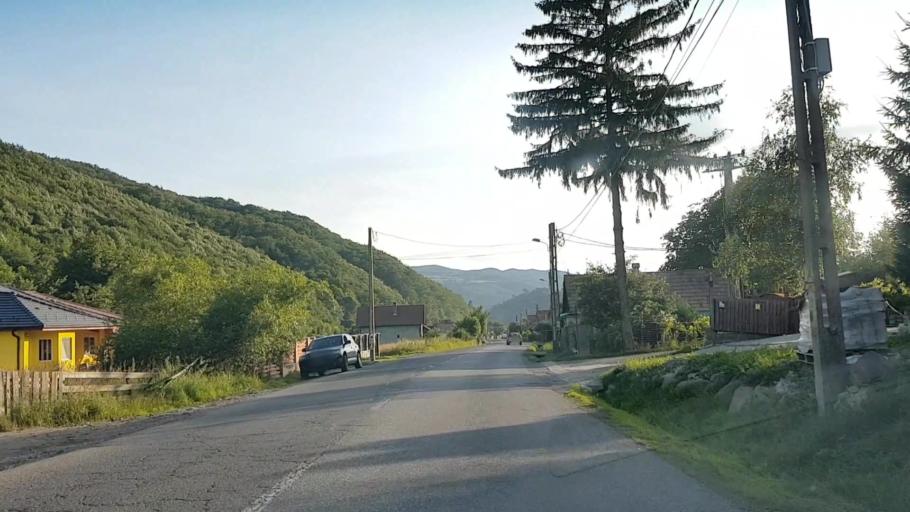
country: RO
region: Harghita
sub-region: Comuna Praid
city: Praid
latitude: 46.5625
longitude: 25.1494
